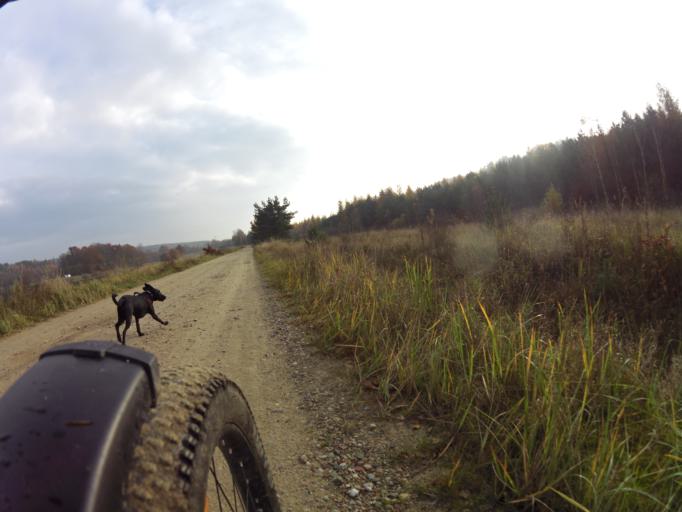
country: PL
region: Pomeranian Voivodeship
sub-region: Powiat wejherowski
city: Orle
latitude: 54.7008
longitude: 18.1105
